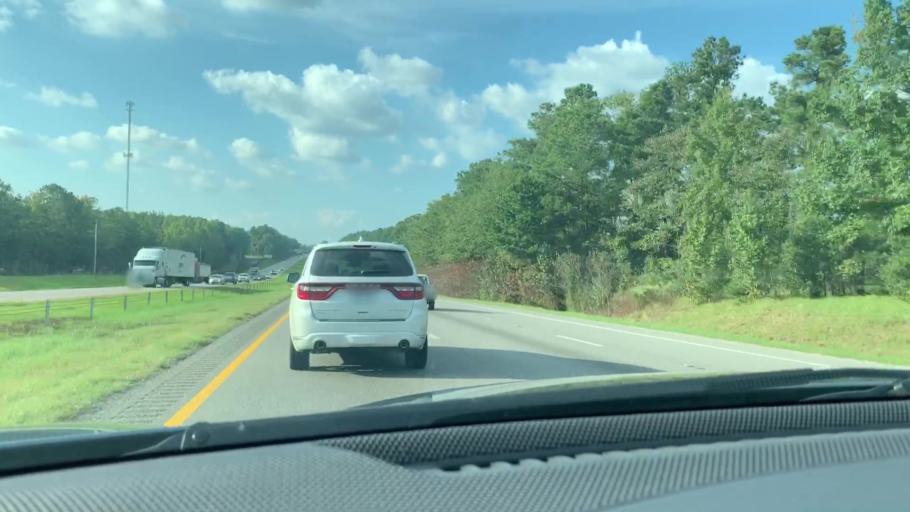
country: US
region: South Carolina
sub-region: Calhoun County
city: Saint Matthews
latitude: 33.6753
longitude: -80.8996
